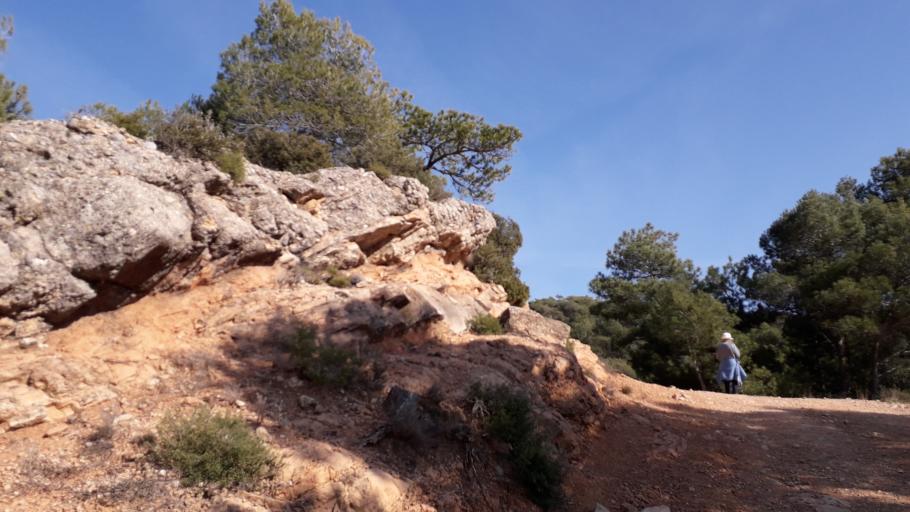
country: ES
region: Catalonia
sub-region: Provincia de Barcelona
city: Sant Marti de Tous
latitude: 41.5201
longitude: 1.4904
